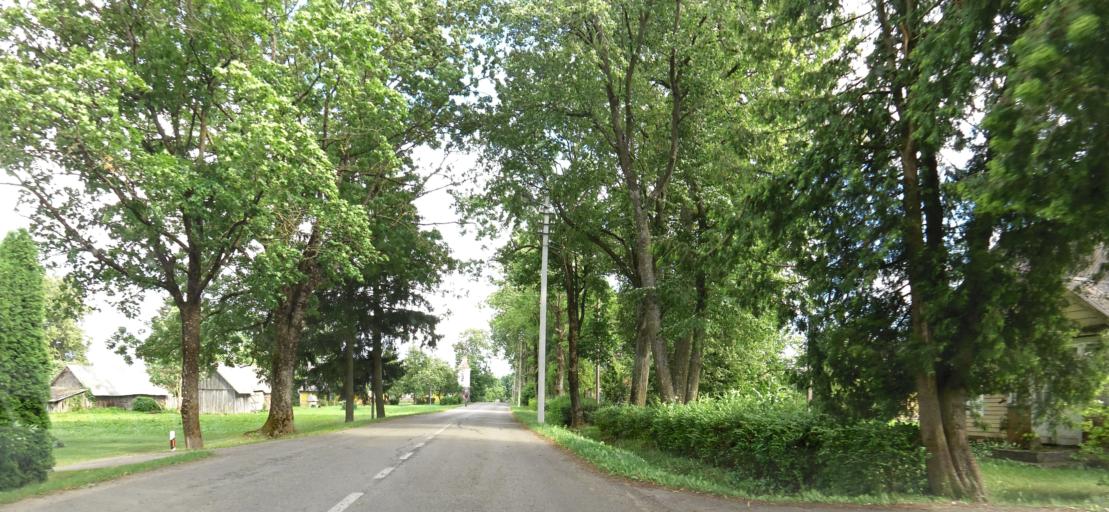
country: LT
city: Obeliai
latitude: 55.8901
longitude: 25.1972
